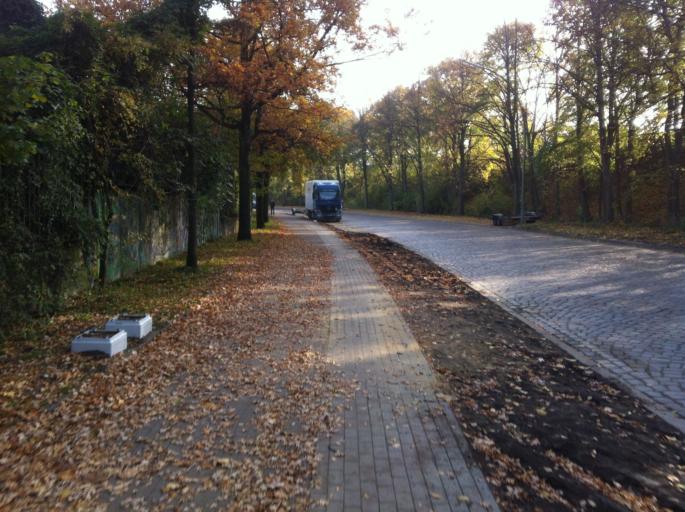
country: DE
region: Hamburg
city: Altona
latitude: 53.5656
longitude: 9.9304
